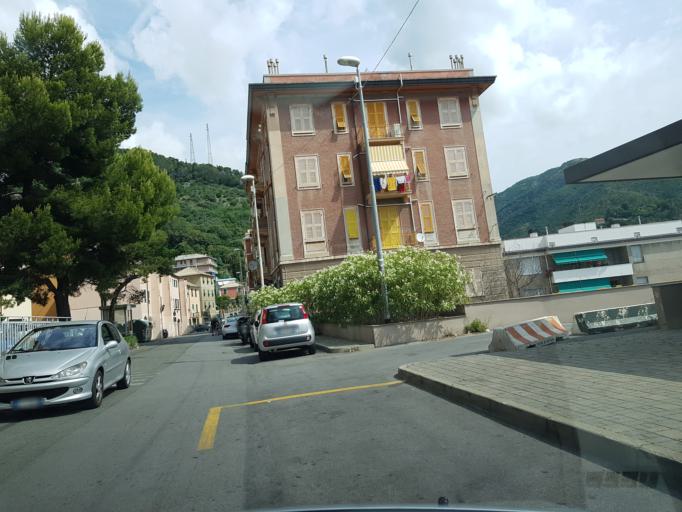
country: IT
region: Liguria
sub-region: Provincia di Genova
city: San Teodoro
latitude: 44.4325
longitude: 8.8517
